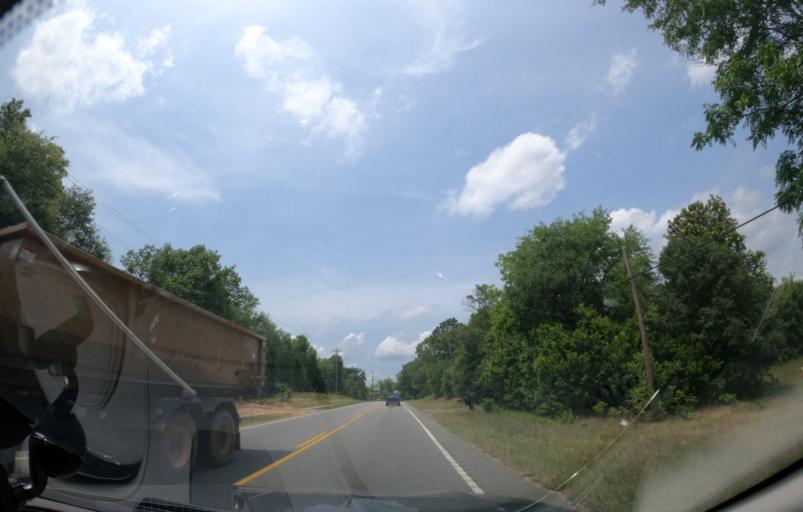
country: US
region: South Carolina
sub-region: Aiken County
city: Aiken
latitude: 33.5885
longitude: -81.7220
